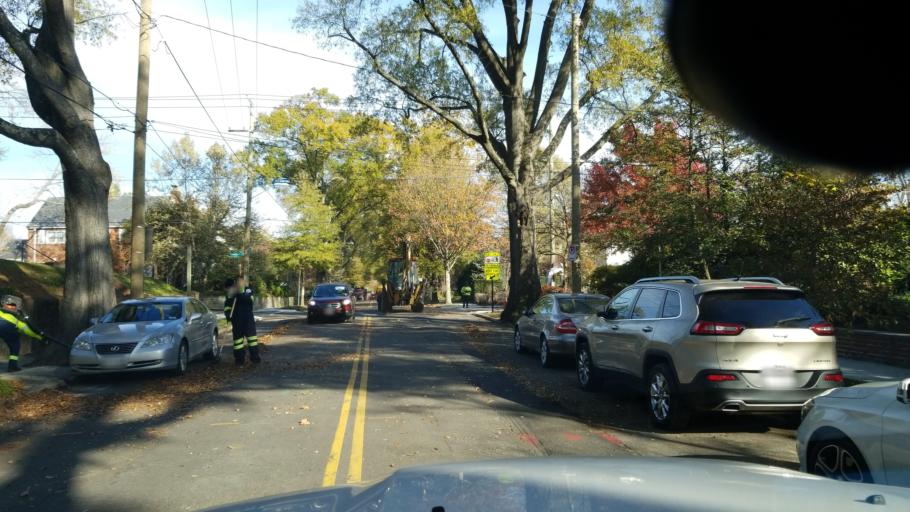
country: US
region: Maryland
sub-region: Montgomery County
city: Friendship Village
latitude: 38.9517
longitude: -77.0906
